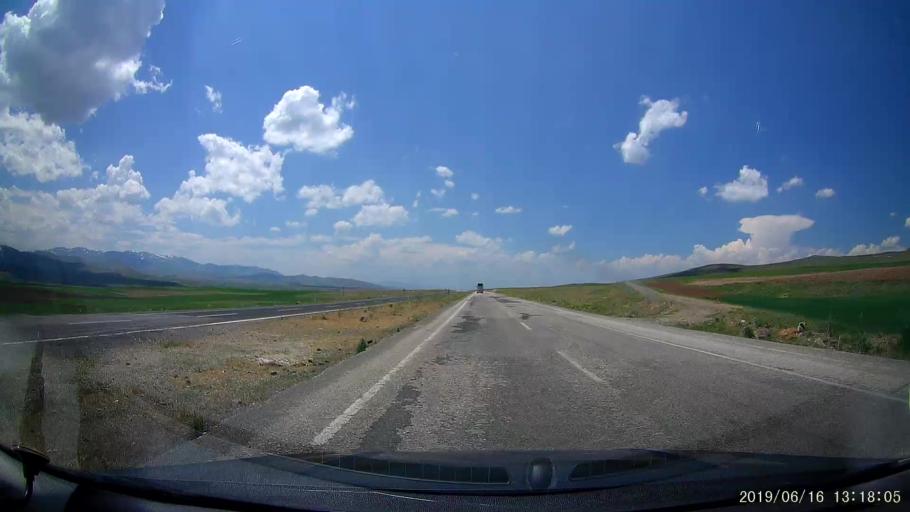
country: TR
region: Agri
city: Taslicay
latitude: 39.6293
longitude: 43.4386
